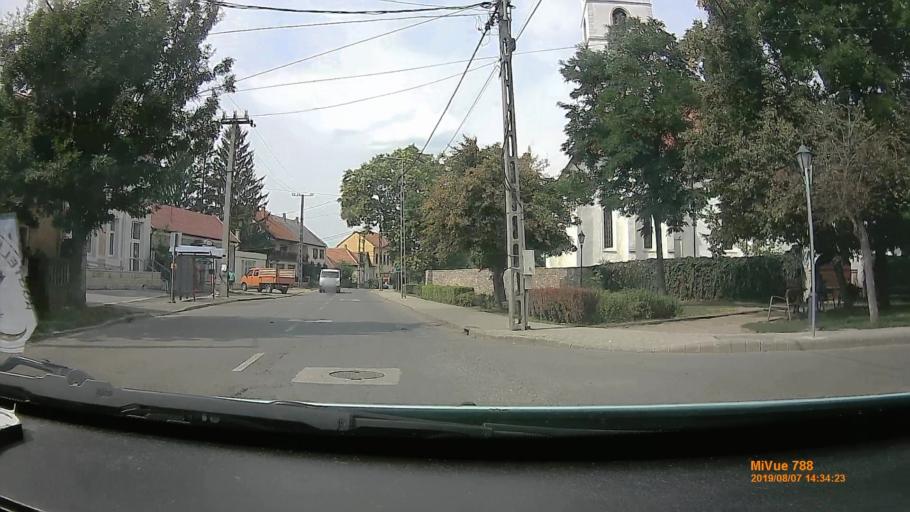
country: HU
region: Borsod-Abauj-Zemplen
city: Szikszo
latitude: 48.2007
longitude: 20.9270
